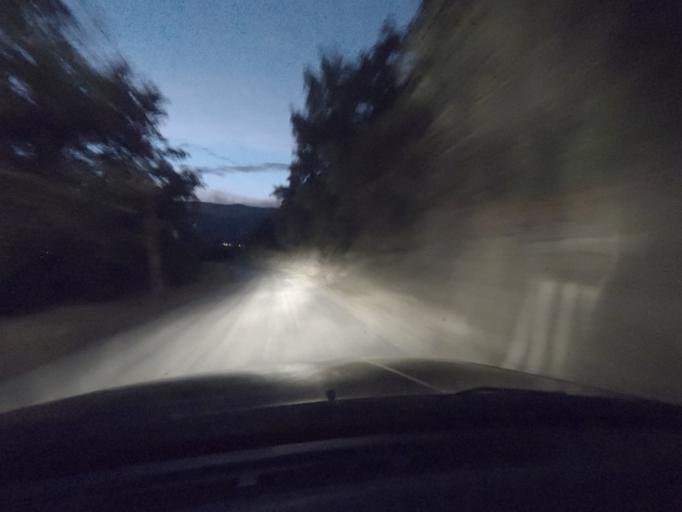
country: PT
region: Vila Real
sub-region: Peso da Regua
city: Godim
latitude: 41.1845
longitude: -7.8355
